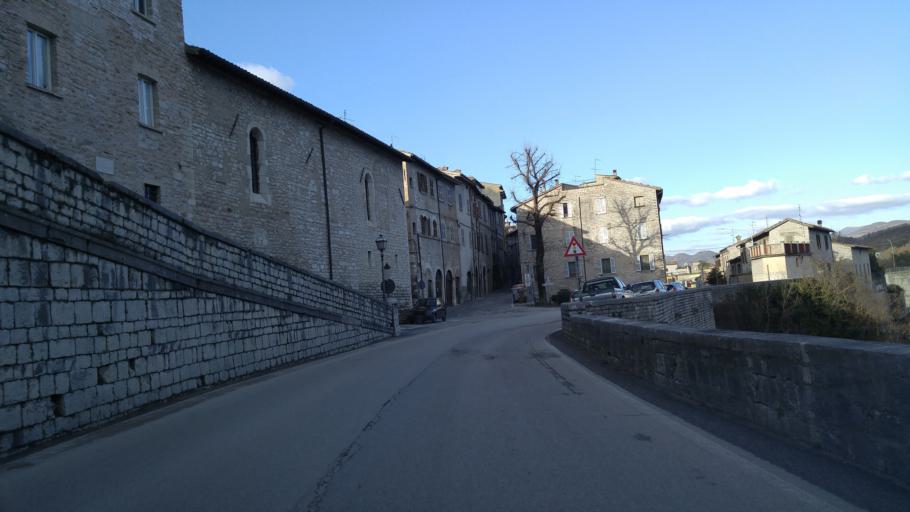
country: IT
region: The Marches
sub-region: Provincia di Pesaro e Urbino
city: Cagli
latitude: 43.5444
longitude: 12.6494
